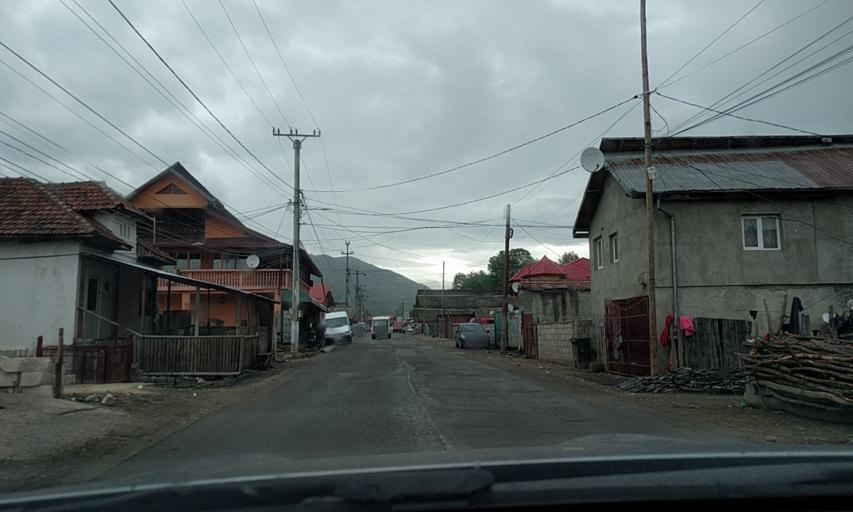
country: RO
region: Dambovita
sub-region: Comuna Moroeni
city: Glod
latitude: 45.2382
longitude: 25.4468
